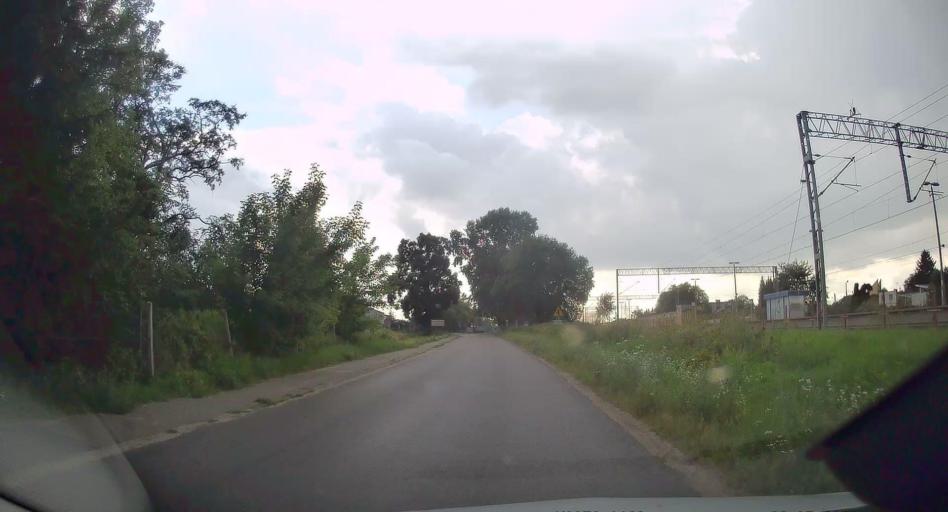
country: PL
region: Lodz Voivodeship
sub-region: Powiat brzezinski
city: Rogow
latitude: 51.8191
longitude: 19.8881
